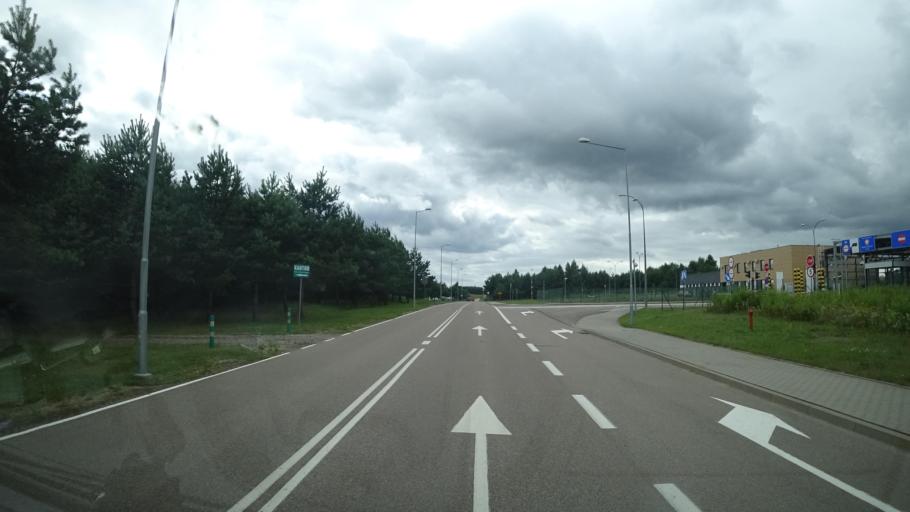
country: PL
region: Warmian-Masurian Voivodeship
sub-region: Powiat goldapski
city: Goldap
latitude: 54.3375
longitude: 22.2947
